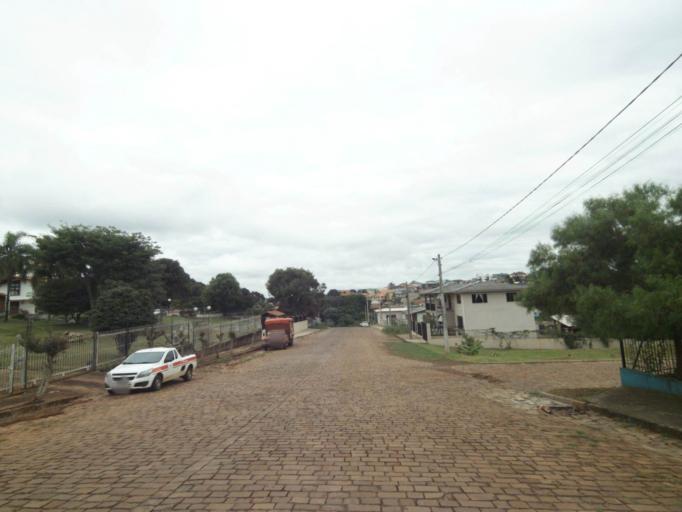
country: BR
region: Rio Grande do Sul
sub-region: Lagoa Vermelha
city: Lagoa Vermelha
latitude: -28.2148
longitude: -51.5267
